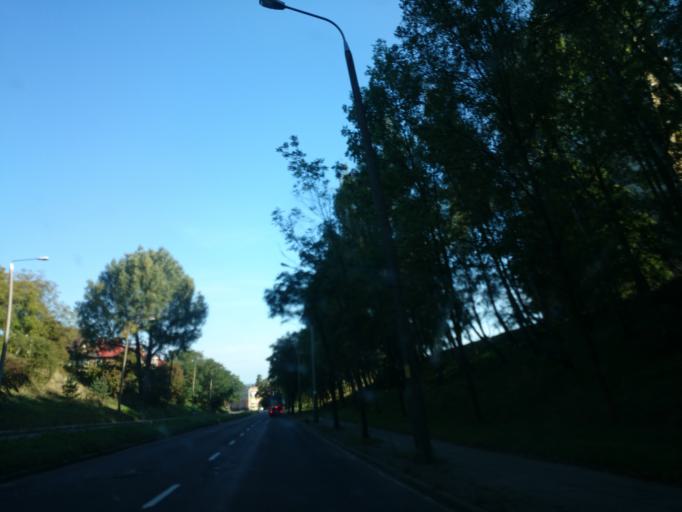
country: PL
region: Lubusz
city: Gorzow Wielkopolski
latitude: 52.7333
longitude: 15.2149
